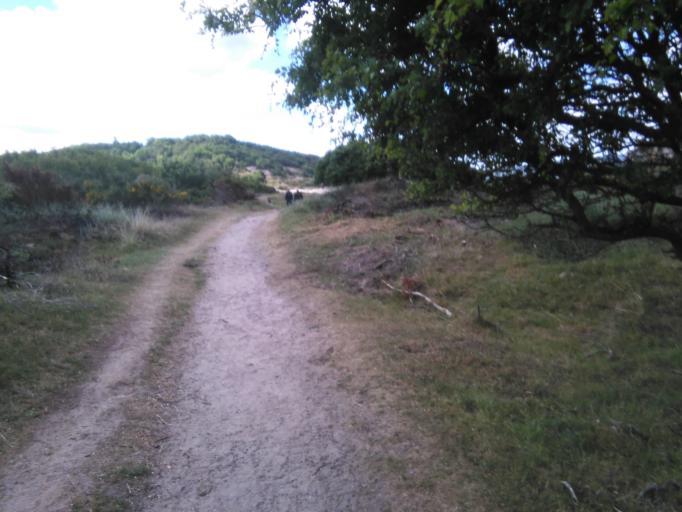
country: DK
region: Capital Region
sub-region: Bornholm Kommune
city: Ronne
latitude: 55.2942
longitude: 14.7644
